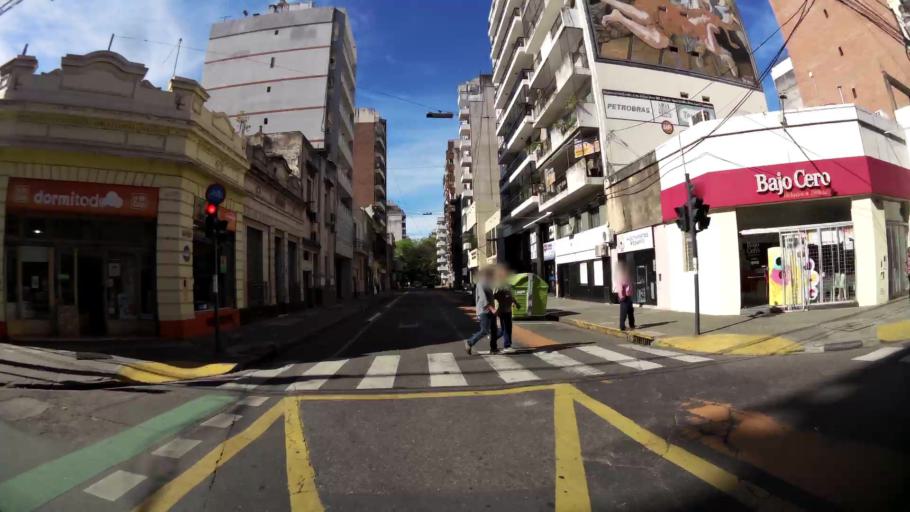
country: AR
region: Santa Fe
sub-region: Departamento de Rosario
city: Rosario
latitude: -32.9511
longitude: -60.6425
